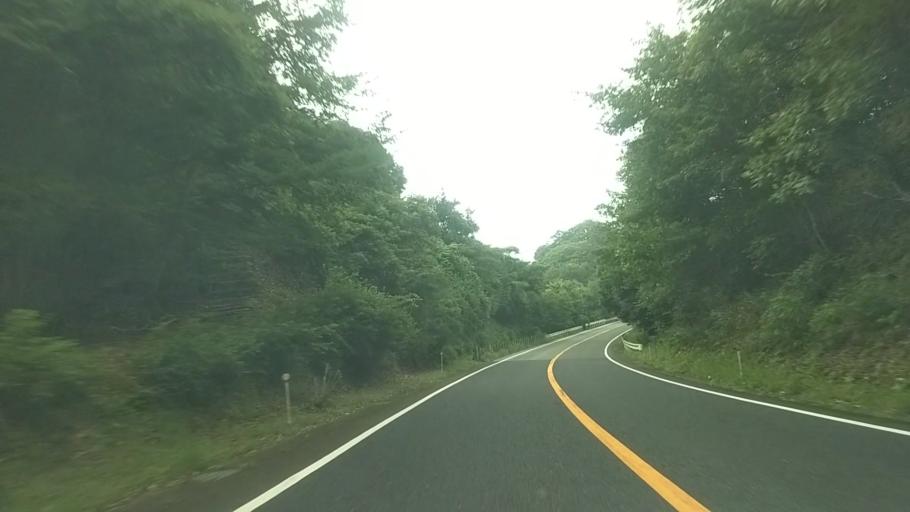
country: JP
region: Chiba
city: Kawaguchi
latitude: 35.2183
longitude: 140.0391
